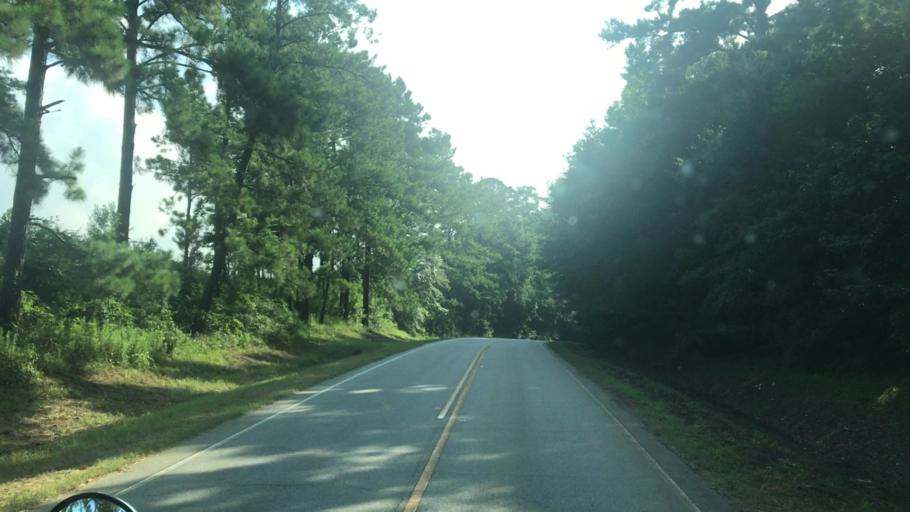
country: US
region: Florida
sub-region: Gadsden County
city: Havana
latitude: 30.7160
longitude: -84.4966
